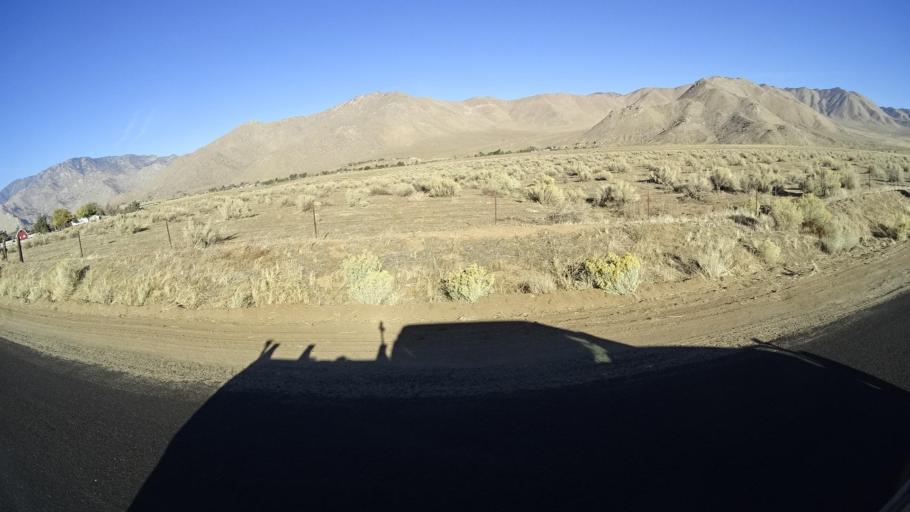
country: US
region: California
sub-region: Kern County
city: Weldon
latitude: 35.6252
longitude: -118.2617
